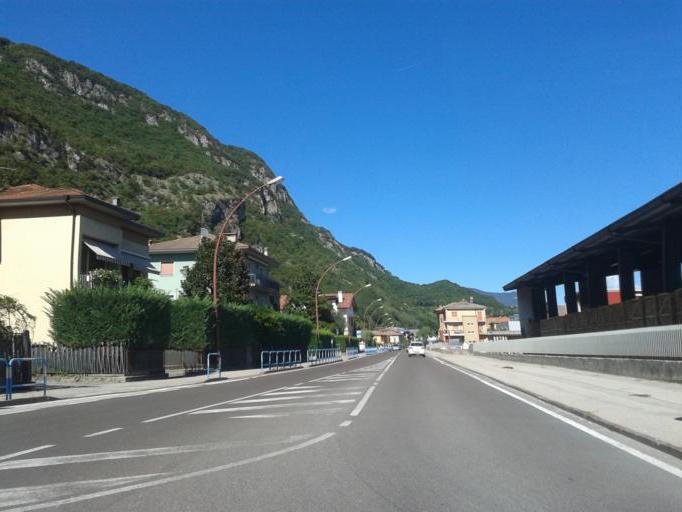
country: IT
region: Trentino-Alto Adige
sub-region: Provincia di Trento
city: Mori
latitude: 45.8572
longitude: 10.9896
